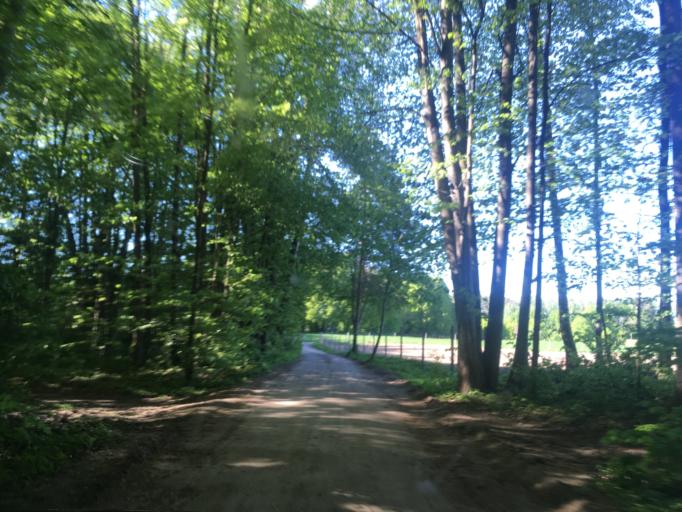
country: PL
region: Warmian-Masurian Voivodeship
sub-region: Powiat piski
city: Ruciane-Nida
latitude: 53.6529
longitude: 21.4849
